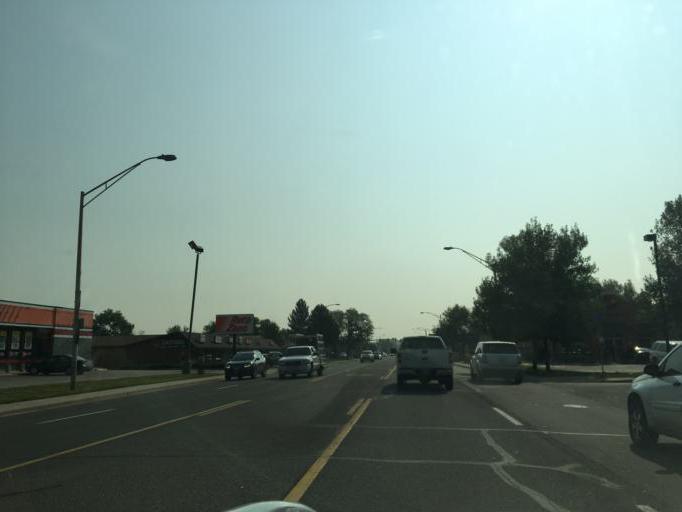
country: US
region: Colorado
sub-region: Adams County
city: Brighton
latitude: 39.9867
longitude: -104.8117
